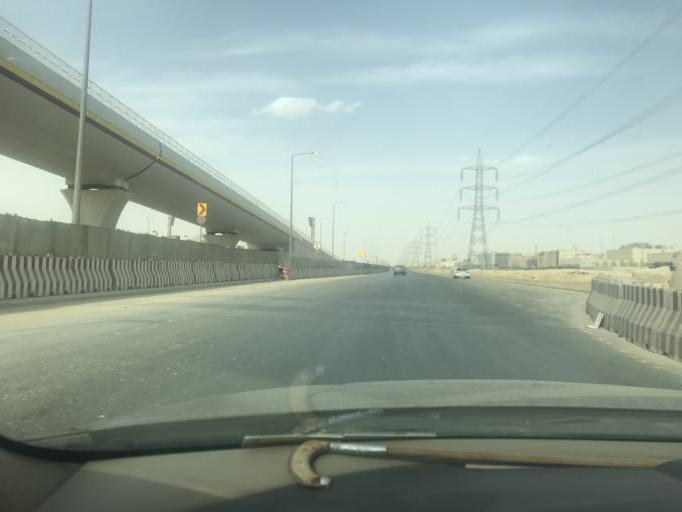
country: SA
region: Ar Riyad
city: Riyadh
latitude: 24.8021
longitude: 46.6979
